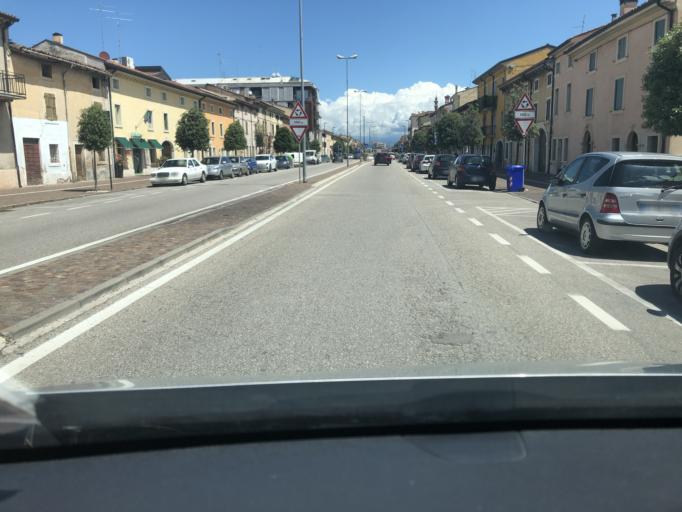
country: IT
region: Veneto
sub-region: Provincia di Verona
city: Villafranca di Verona
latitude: 45.3520
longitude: 10.8405
